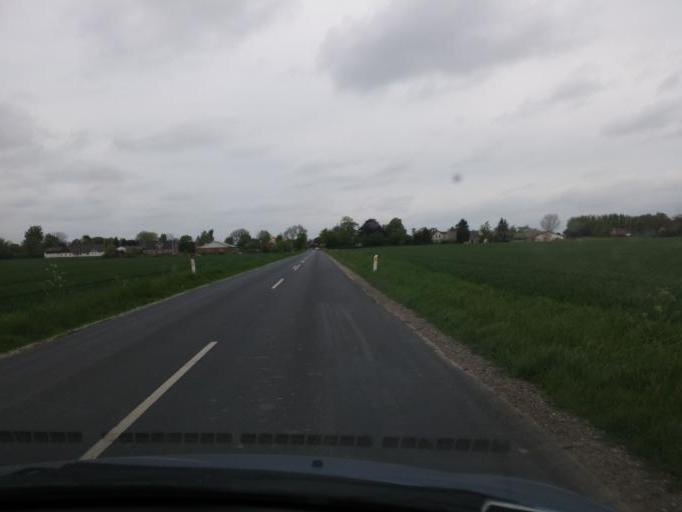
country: DK
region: South Denmark
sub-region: Kerteminde Kommune
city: Kerteminde
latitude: 55.4282
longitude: 10.6163
